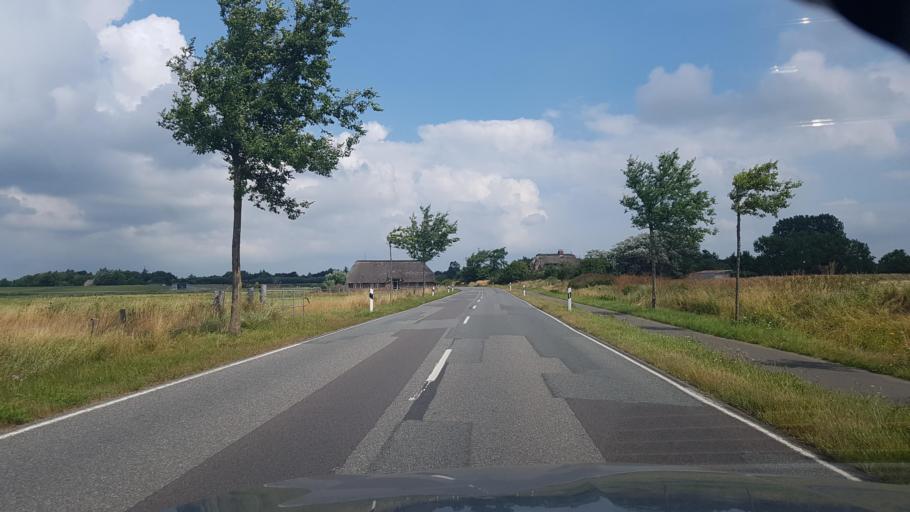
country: DE
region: Schleswig-Holstein
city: Schobull
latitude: 54.5172
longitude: 8.9950
